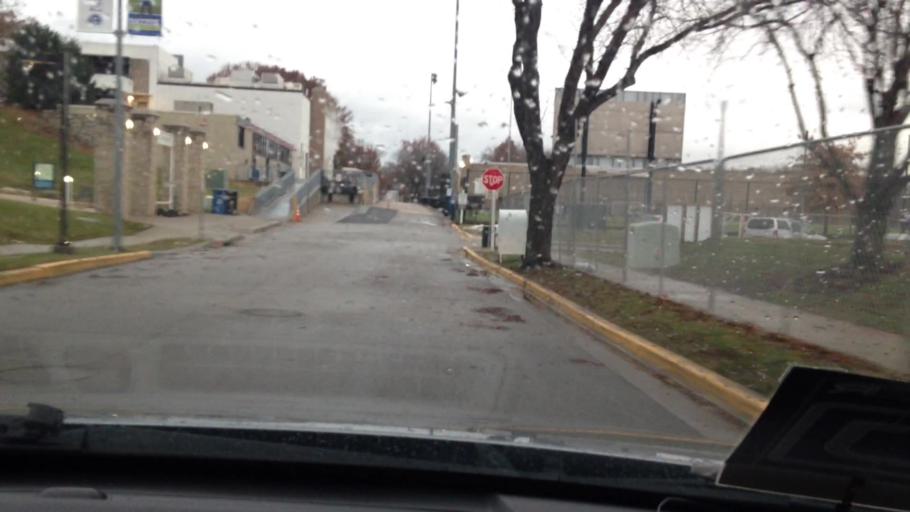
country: US
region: Kansas
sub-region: Johnson County
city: Westwood
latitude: 39.0304
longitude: -94.5713
